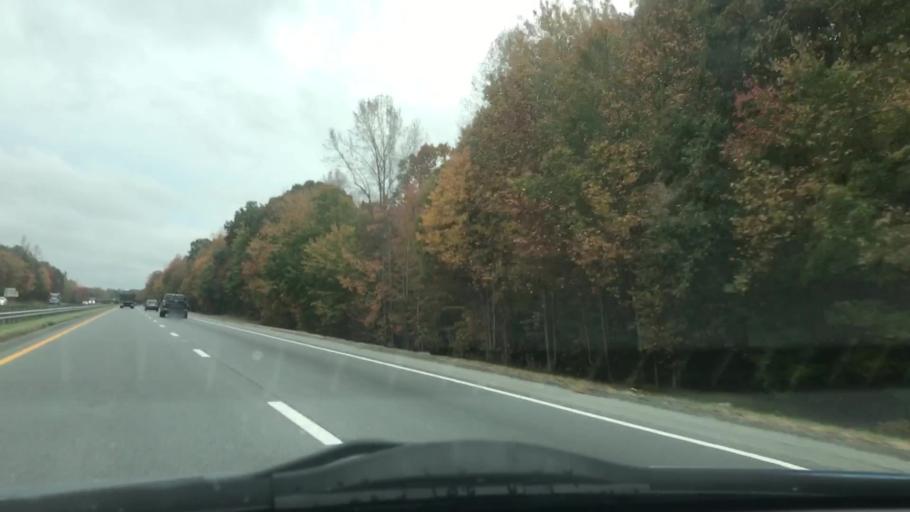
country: US
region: North Carolina
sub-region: Randolph County
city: Asheboro
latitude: 35.7401
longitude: -79.8252
